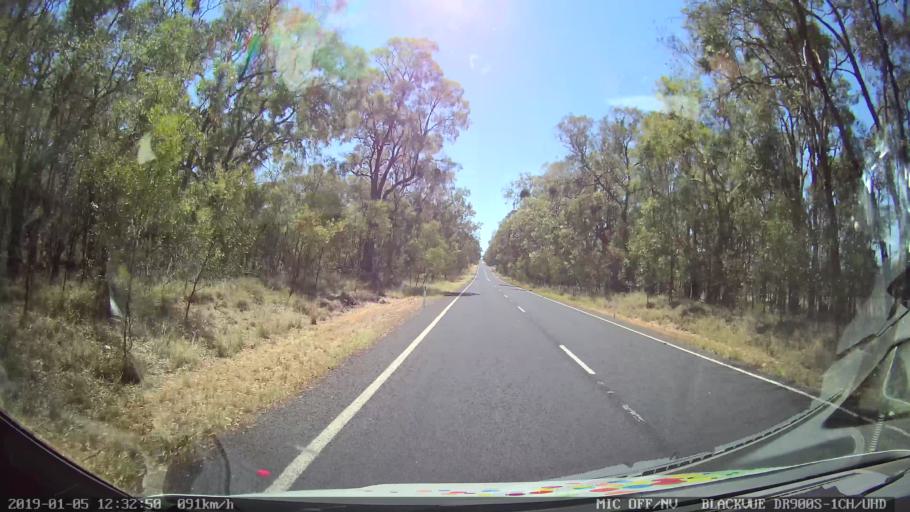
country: AU
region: New South Wales
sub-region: Warrumbungle Shire
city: Coonabarabran
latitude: -31.2163
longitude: 149.3858
